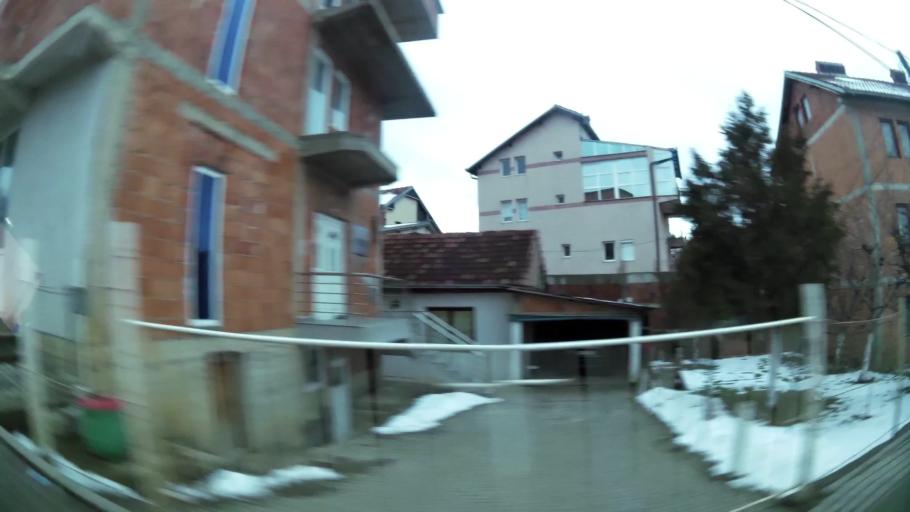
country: XK
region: Pristina
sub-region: Komuna e Prishtines
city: Pristina
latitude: 42.6422
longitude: 21.1650
